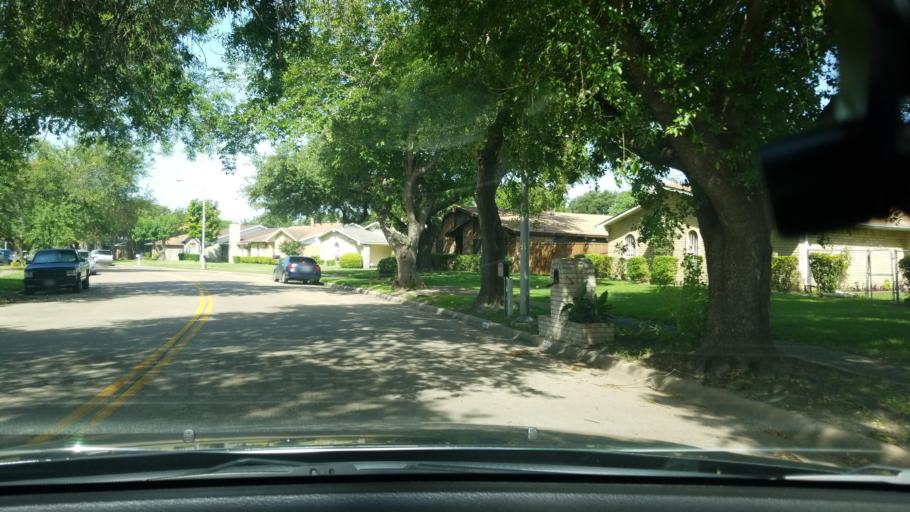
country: US
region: Texas
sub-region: Dallas County
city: Mesquite
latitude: 32.8028
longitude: -96.6924
